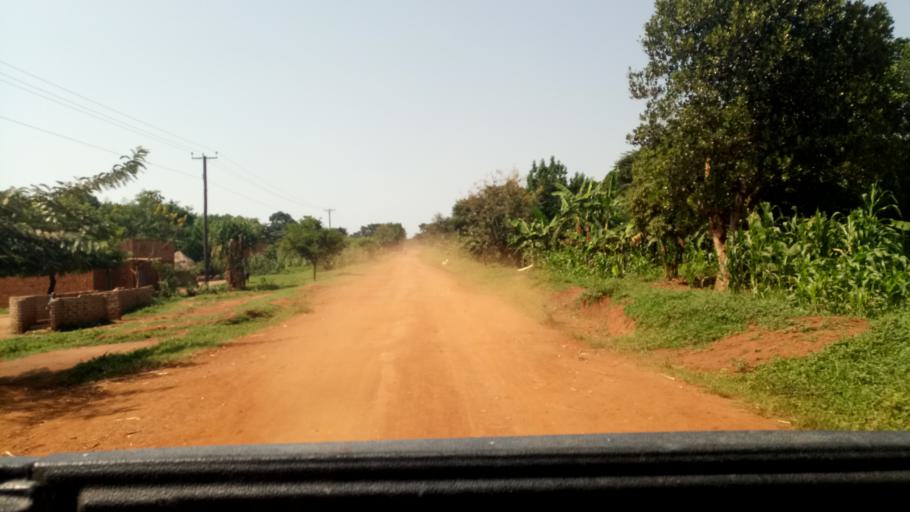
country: UG
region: Eastern Region
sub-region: Kaliro District
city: Kaliro
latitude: 0.9655
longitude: 33.4674
